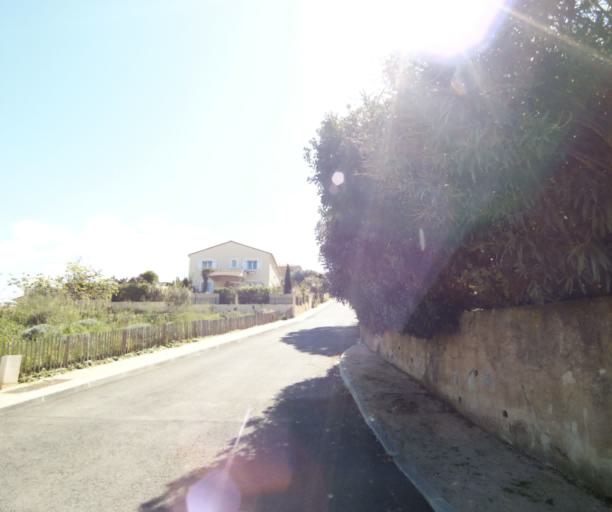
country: FR
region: Corsica
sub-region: Departement de la Corse-du-Sud
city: Propriano
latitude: 41.6749
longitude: 8.9091
